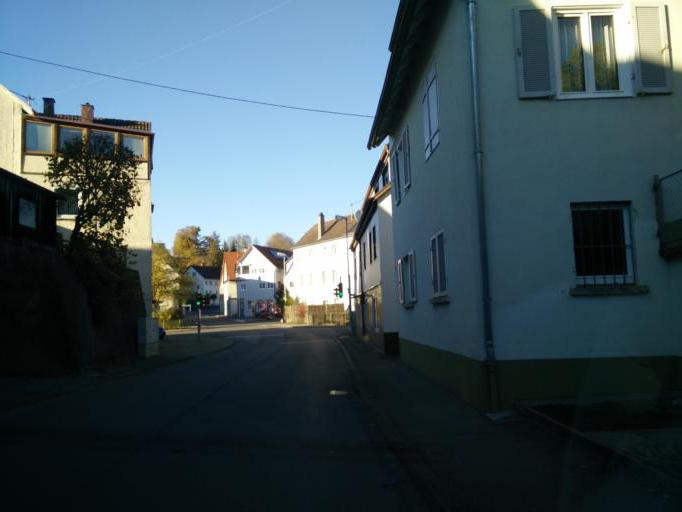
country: DE
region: Baden-Wuerttemberg
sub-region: Tuebingen Region
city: Gomaringen
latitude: 48.4532
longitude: 9.1006
